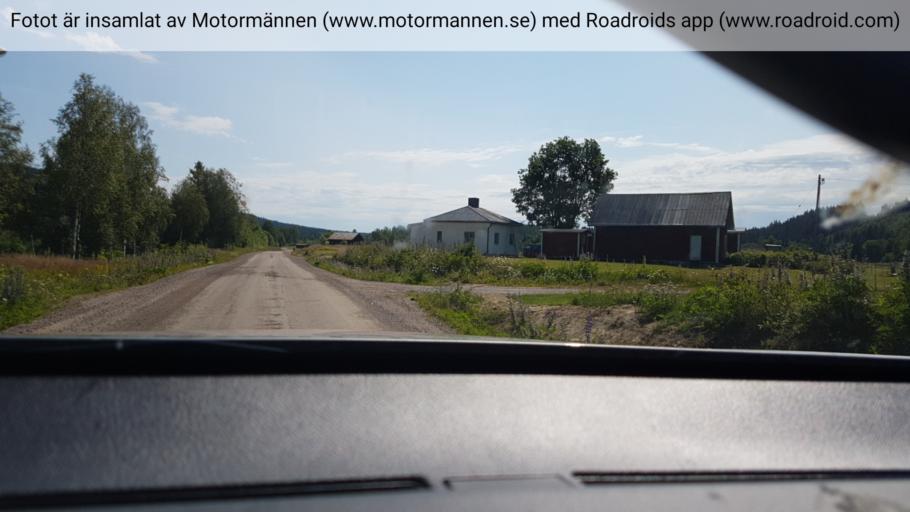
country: SE
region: Vaermland
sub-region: Torsby Kommun
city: Torsby
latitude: 60.5122
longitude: 13.1374
